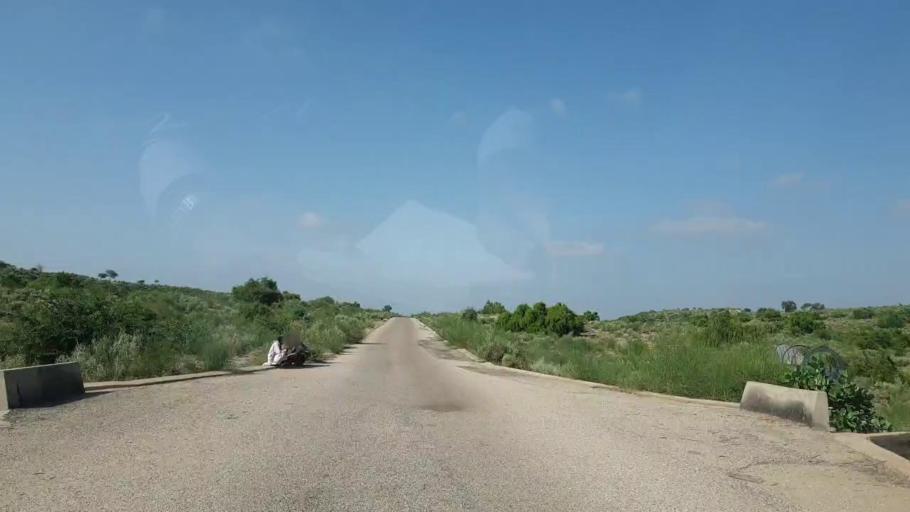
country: PK
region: Sindh
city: Mithi
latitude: 24.5639
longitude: 69.9104
